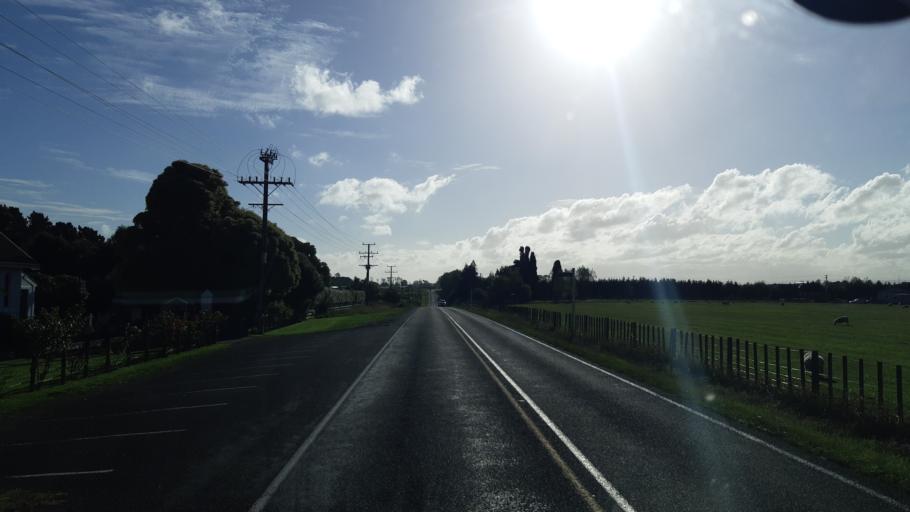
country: NZ
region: Manawatu-Wanganui
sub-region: Wanganui District
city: Wanganui
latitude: -39.9470
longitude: 175.1459
